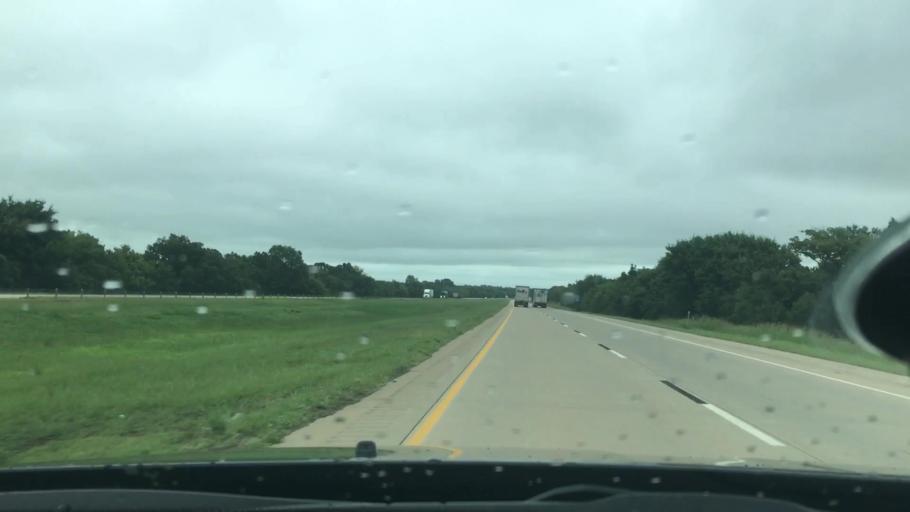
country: US
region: Oklahoma
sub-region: McIntosh County
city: Checotah
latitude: 35.4558
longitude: -95.6394
